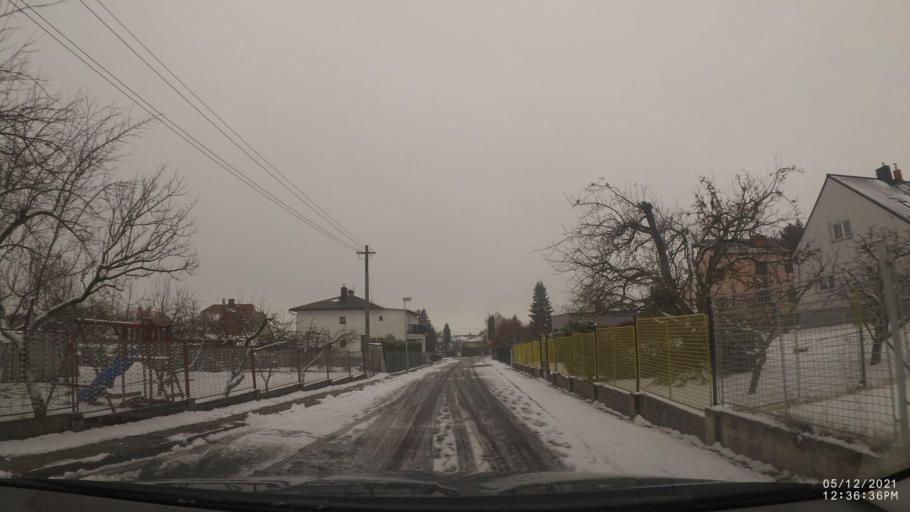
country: CZ
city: Nove Mesto nad Metuji
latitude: 50.3547
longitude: 16.1573
